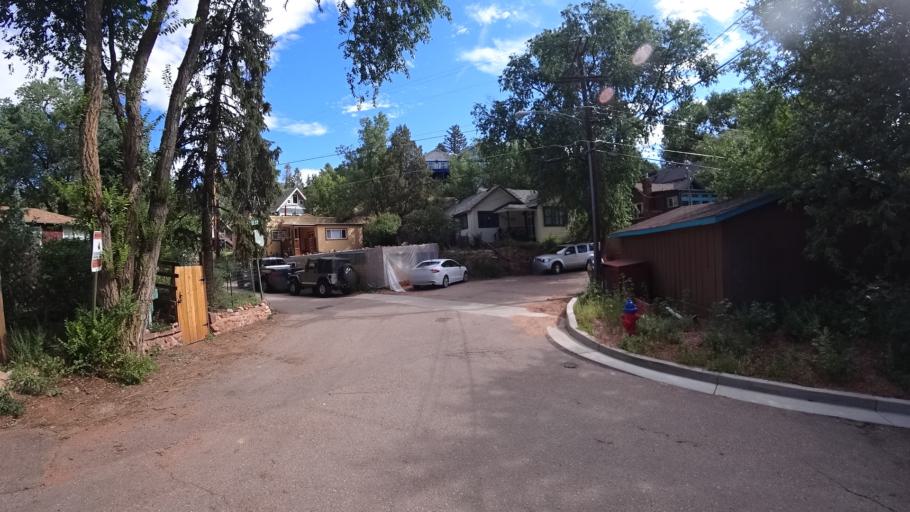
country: US
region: Colorado
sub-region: El Paso County
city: Manitou Springs
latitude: 38.8601
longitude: -104.9242
